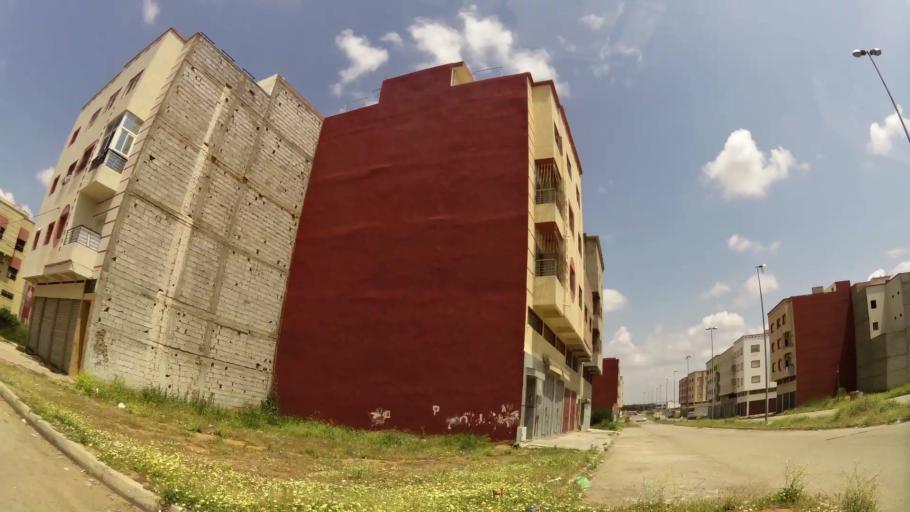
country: MA
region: Gharb-Chrarda-Beni Hssen
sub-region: Kenitra Province
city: Kenitra
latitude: 34.0096
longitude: -6.5372
